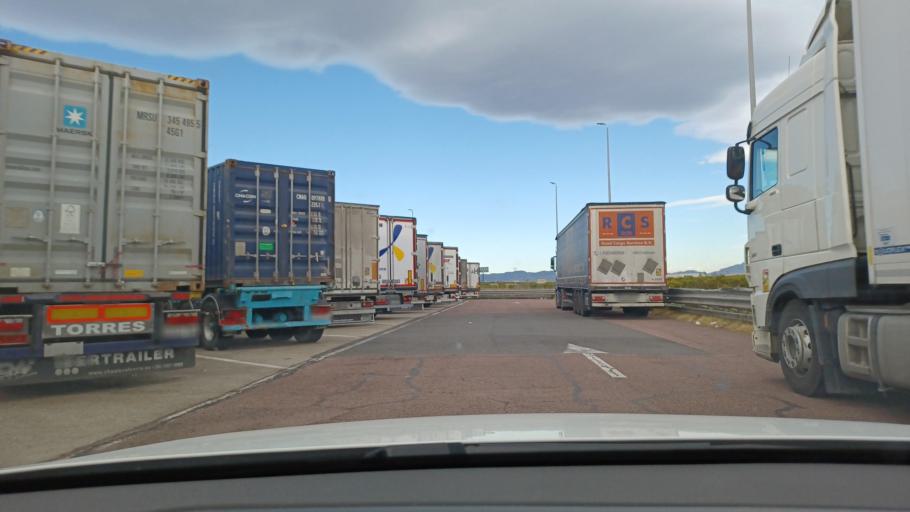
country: ES
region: Valencia
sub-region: Provincia de Castello
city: Alquerias del Nino Perdido
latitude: 39.8647
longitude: -0.1205
